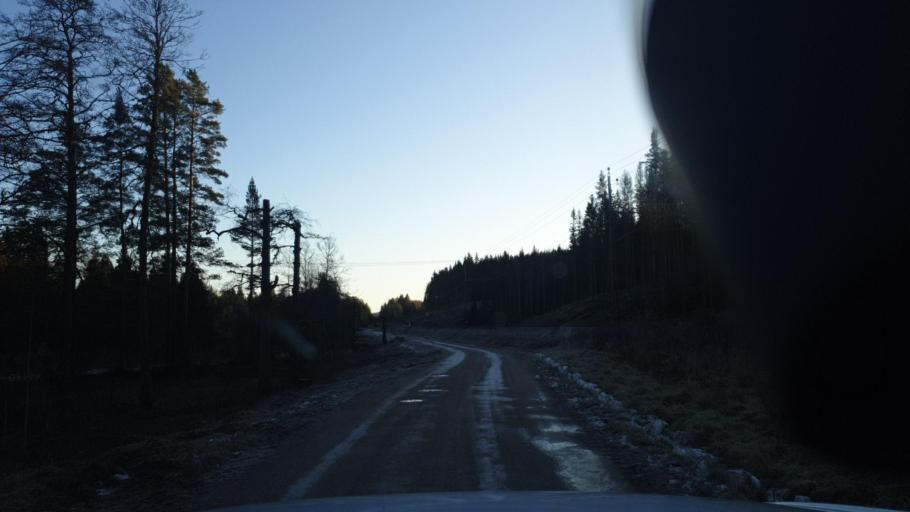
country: SE
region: Vaermland
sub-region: Karlstads Kommun
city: Edsvalla
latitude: 59.6142
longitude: 12.9740
